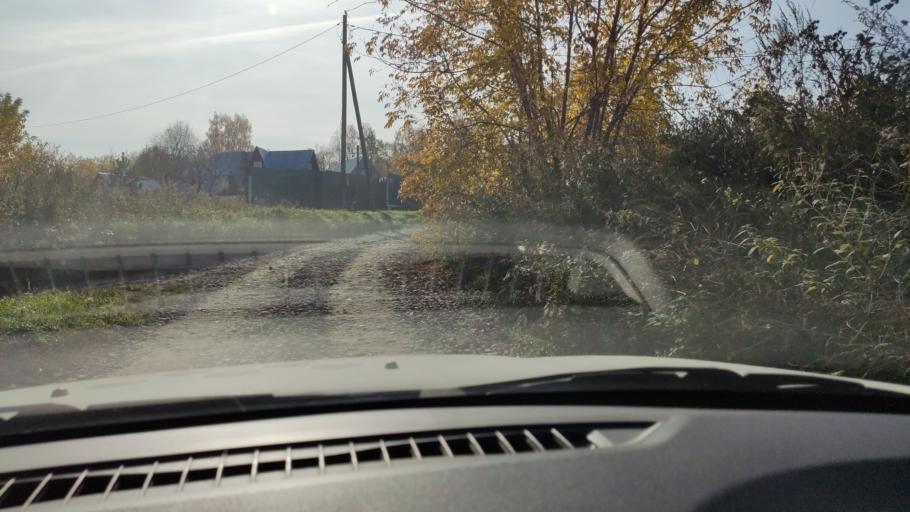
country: RU
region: Perm
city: Sylva
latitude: 58.0466
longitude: 56.7380
